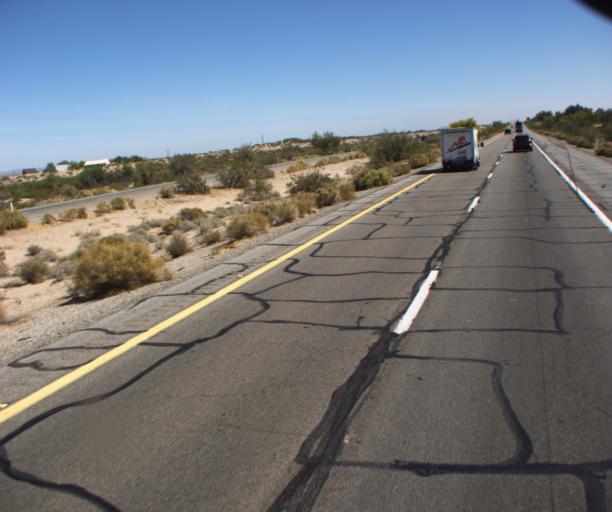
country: US
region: Arizona
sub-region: Yuma County
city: Wellton
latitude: 32.6528
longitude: -114.1800
